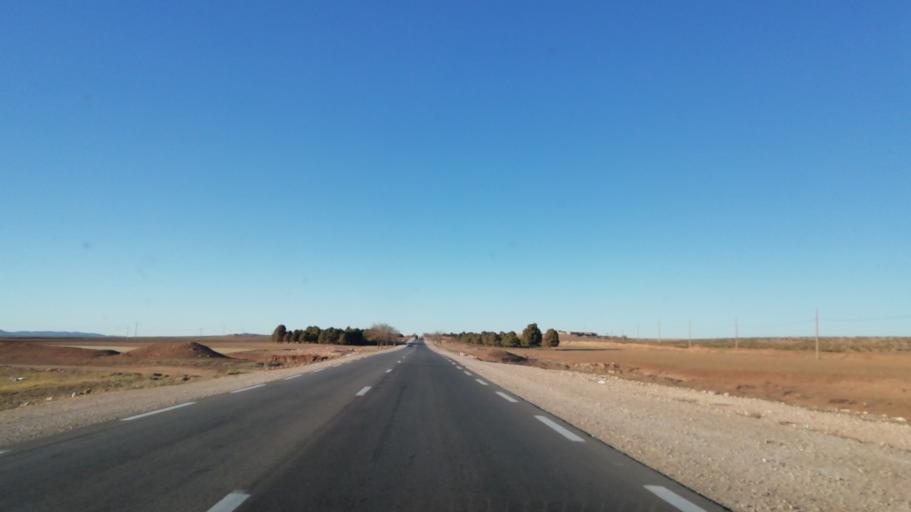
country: DZ
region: Tlemcen
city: Sebdou
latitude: 34.5228
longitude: -1.2903
